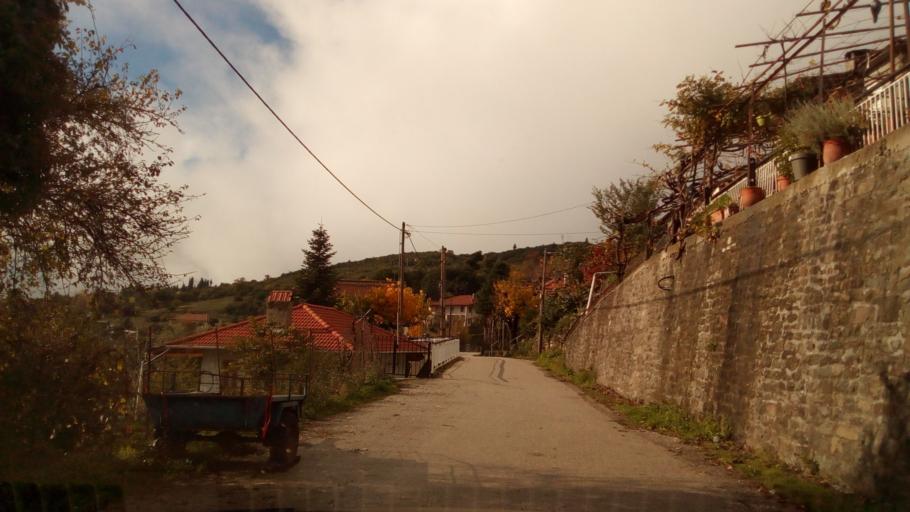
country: GR
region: West Greece
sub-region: Nomos Aitolias kai Akarnanias
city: Nafpaktos
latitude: 38.5426
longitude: 21.9306
